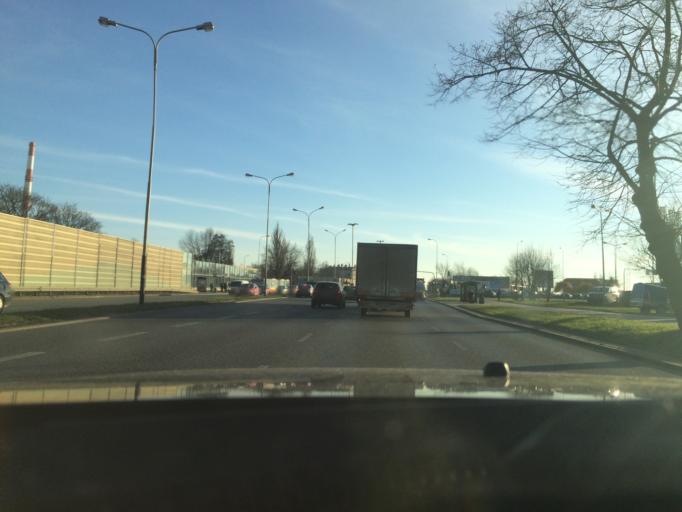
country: PL
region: Lodz Voivodeship
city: Lodz
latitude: 51.7464
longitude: 19.4397
